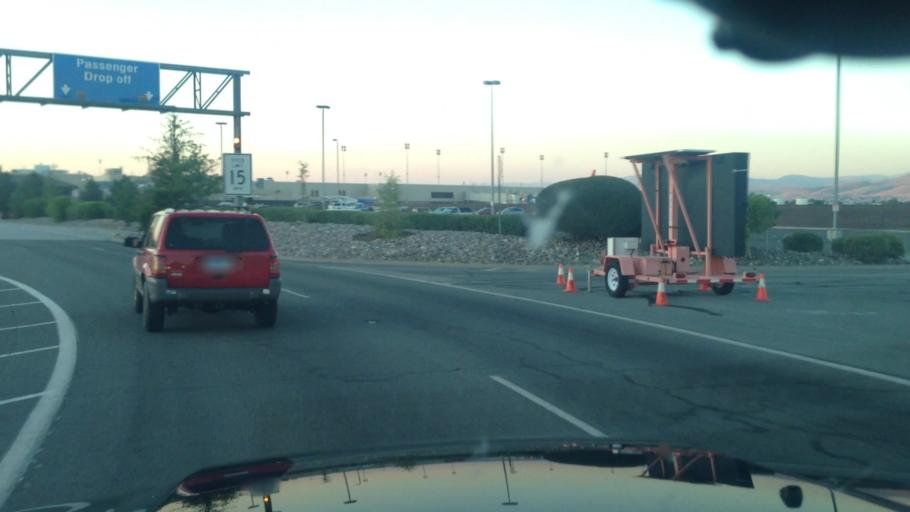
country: US
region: Nevada
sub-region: Washoe County
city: Sparks
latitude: 39.5024
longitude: -119.7759
